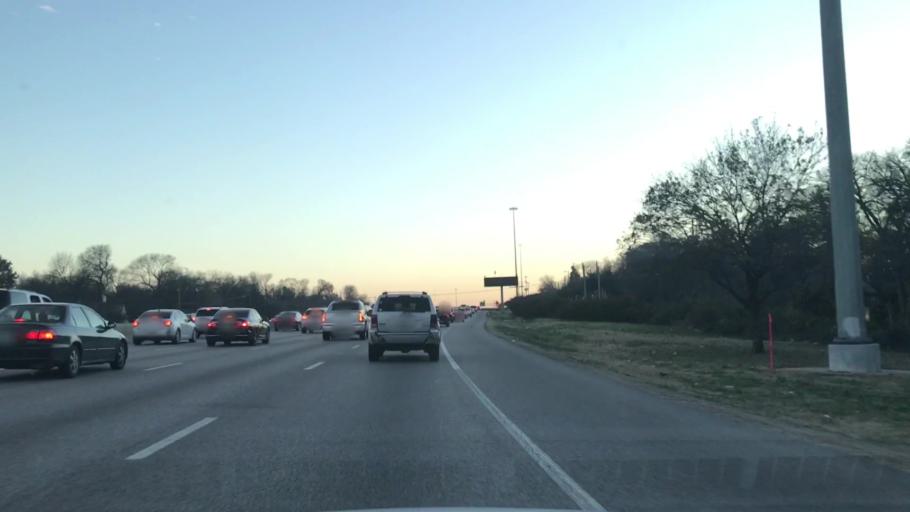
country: US
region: Texas
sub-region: Dallas County
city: Dallas
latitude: 32.7278
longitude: -96.8259
